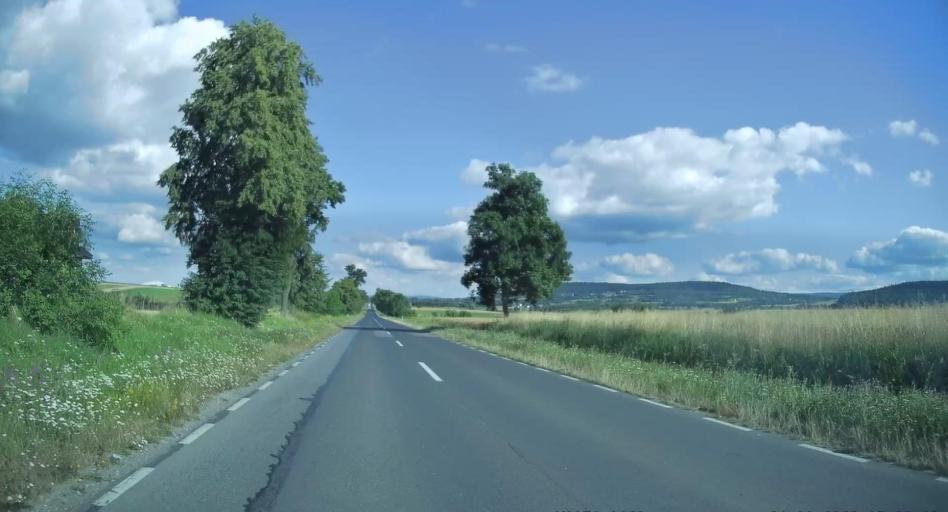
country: PL
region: Swietokrzyskie
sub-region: Powiat kielecki
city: Bodzentyn
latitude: 50.9556
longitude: 20.9159
